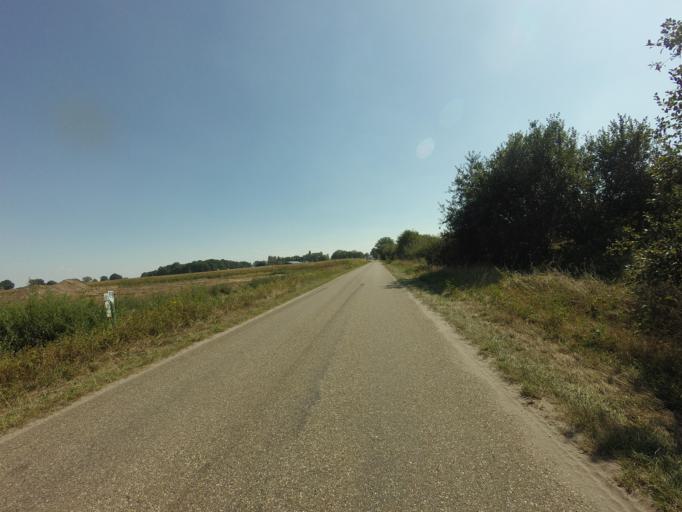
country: NL
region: North Brabant
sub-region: Gemeente Someren
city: Someren
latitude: 51.3811
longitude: 5.6711
